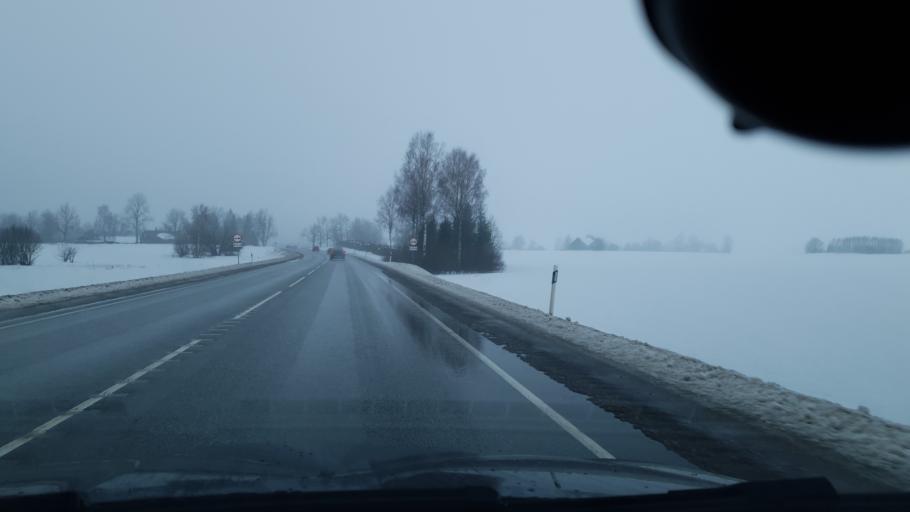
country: EE
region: Jaervamaa
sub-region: Paide linn
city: Paide
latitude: 58.8609
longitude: 25.7161
